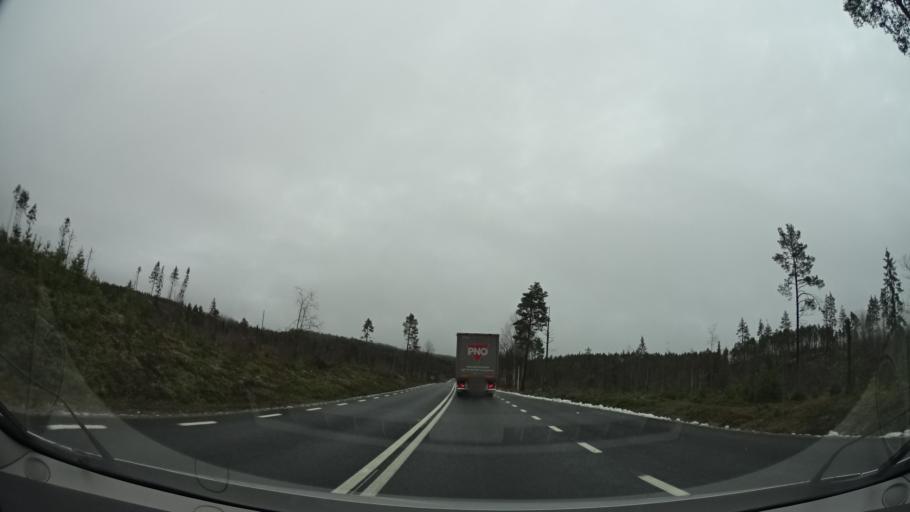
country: SE
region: Vaesterbotten
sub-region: Dorotea Kommun
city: Dorotea
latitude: 64.2338
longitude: 16.3075
